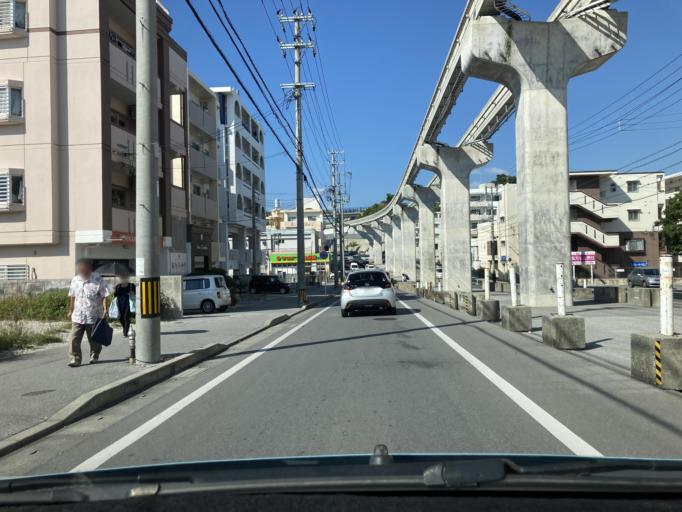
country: JP
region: Okinawa
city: Ginowan
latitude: 26.2326
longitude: 127.7287
